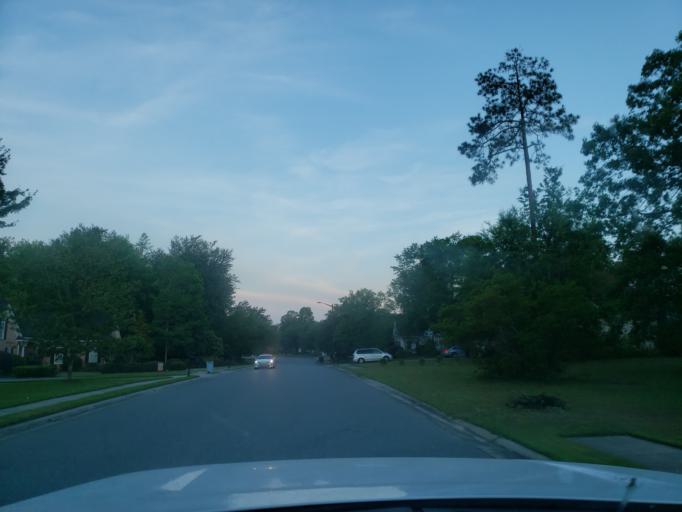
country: US
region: Georgia
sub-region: Chatham County
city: Pooler
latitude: 32.0704
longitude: -81.2423
